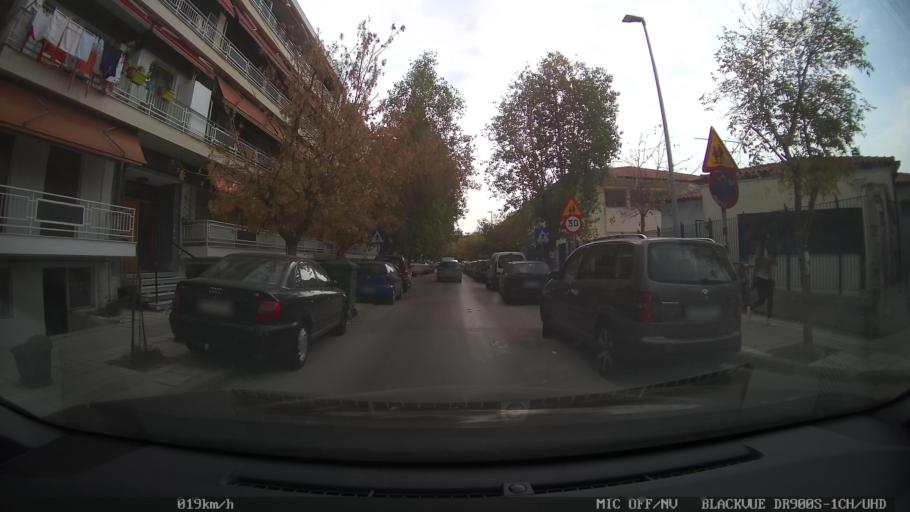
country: GR
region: Central Macedonia
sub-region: Nomos Thessalonikis
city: Triandria
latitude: 40.6108
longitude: 22.9723
